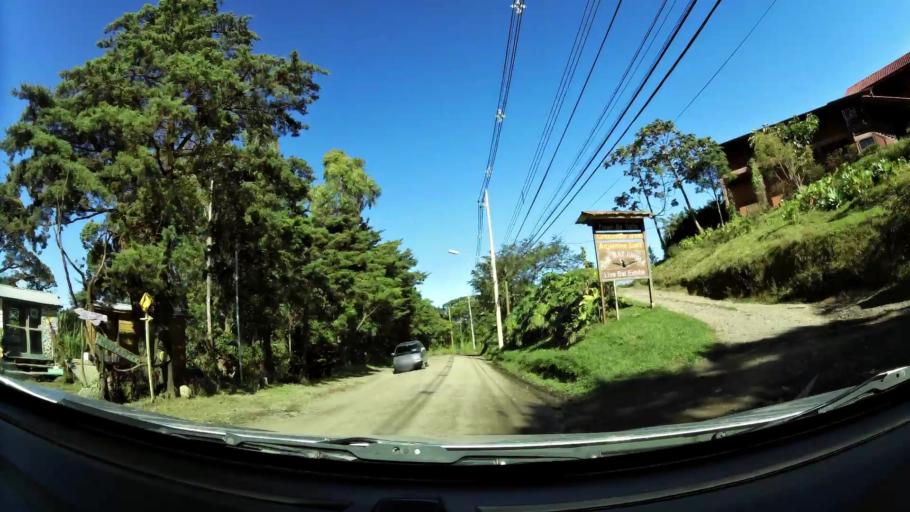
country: CR
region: Guanacaste
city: Juntas
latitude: 10.3077
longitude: -84.8124
